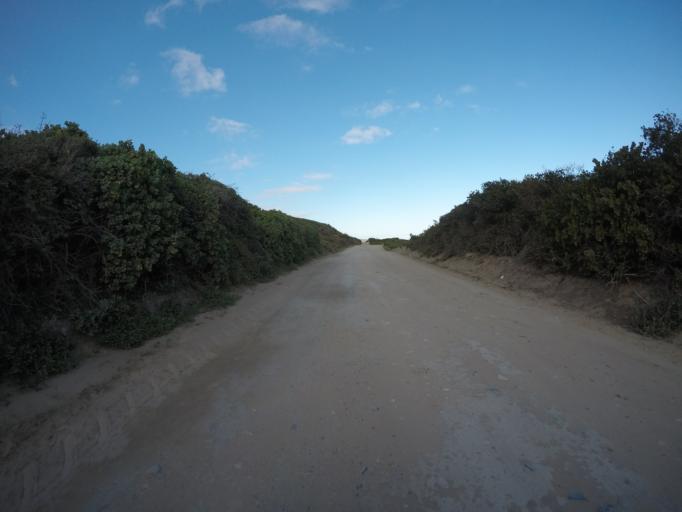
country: ZA
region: Western Cape
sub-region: Eden District Municipality
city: Riversdale
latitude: -34.4187
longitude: 21.3542
